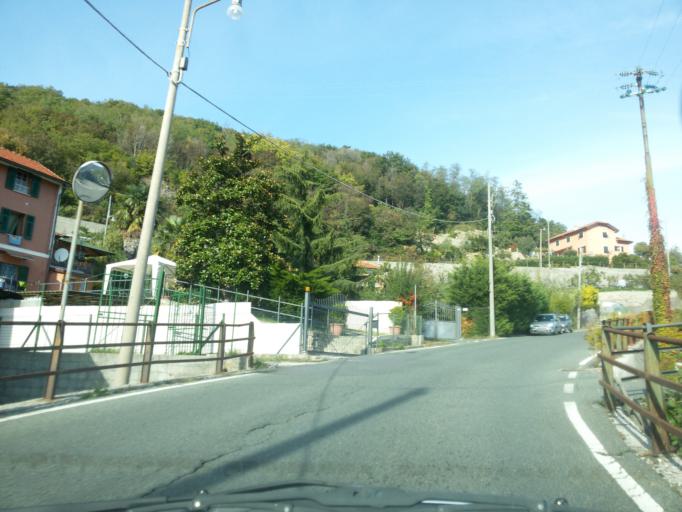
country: IT
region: Liguria
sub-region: Provincia di Genova
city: Piccarello
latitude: 44.4678
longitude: 8.9623
